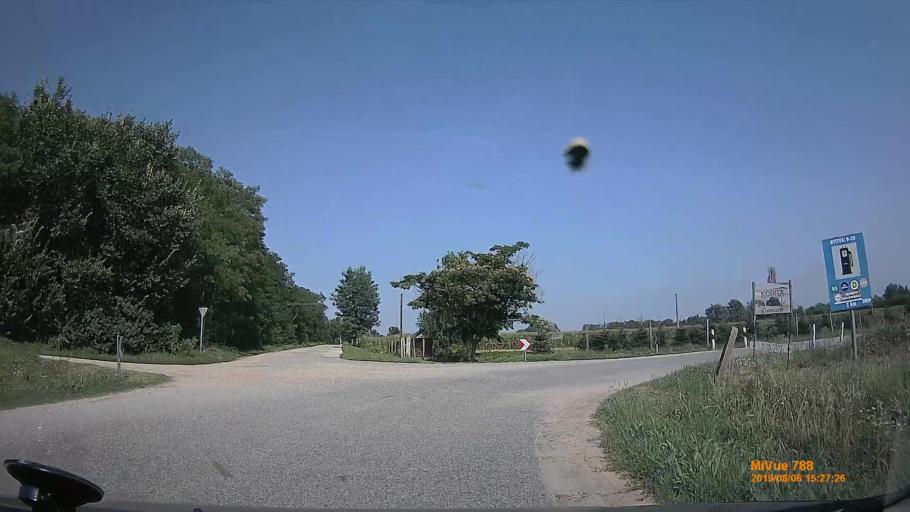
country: HR
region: Koprivnicko-Krizevacka
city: Drnje
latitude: 46.2521
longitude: 16.9694
